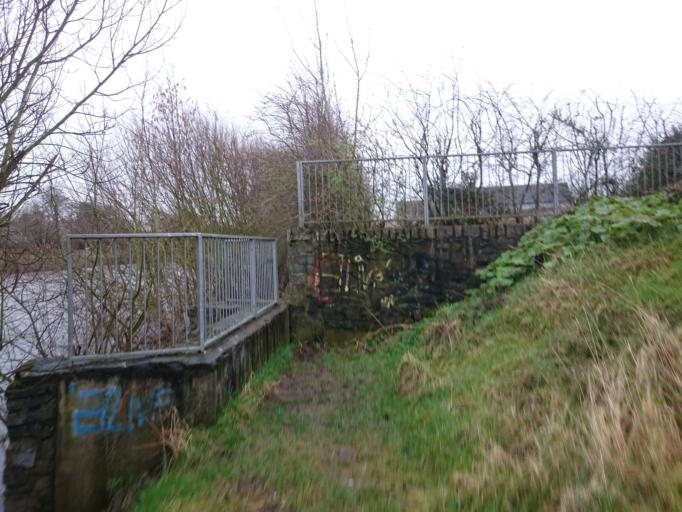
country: IE
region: Leinster
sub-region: Kilkenny
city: Kilkenny
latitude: 52.6590
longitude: -7.2548
